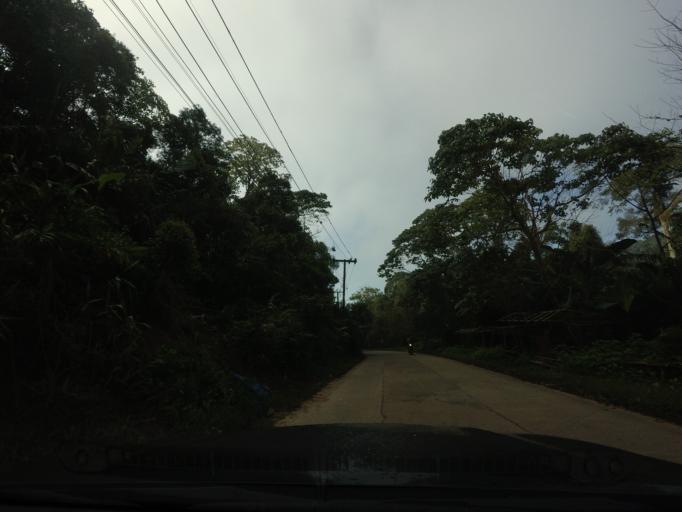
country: TH
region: Phetchabun
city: Lom Kao
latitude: 16.8972
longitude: 101.1044
